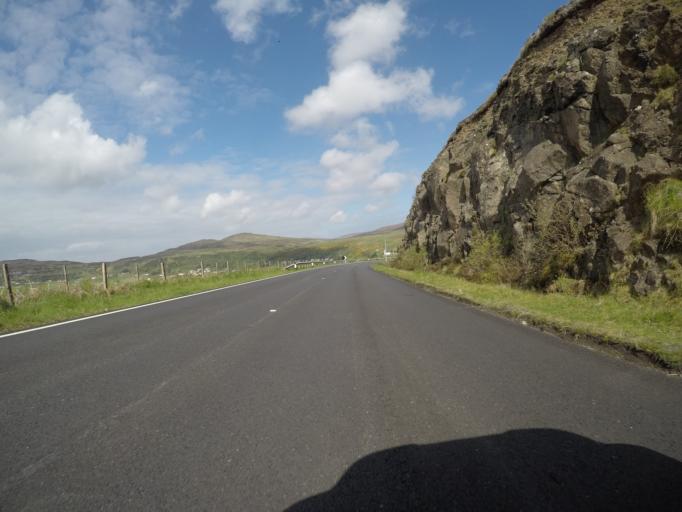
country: GB
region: Scotland
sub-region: Highland
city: Portree
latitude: 57.5799
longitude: -6.3625
